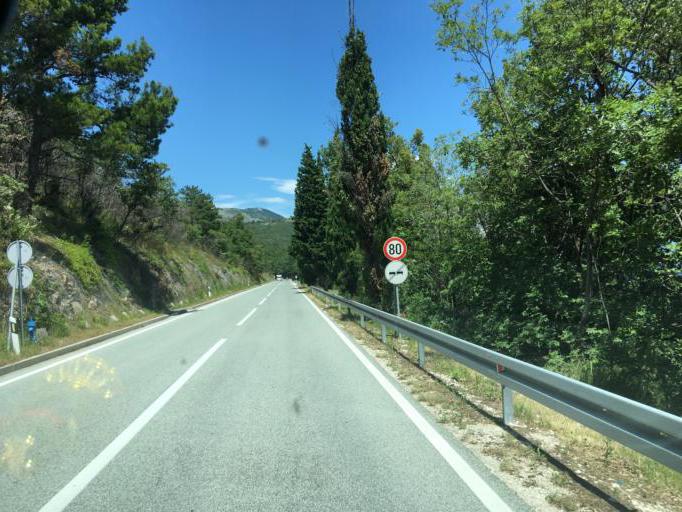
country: HR
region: Istarska
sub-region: Grad Labin
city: Rabac
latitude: 45.1278
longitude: 14.2046
